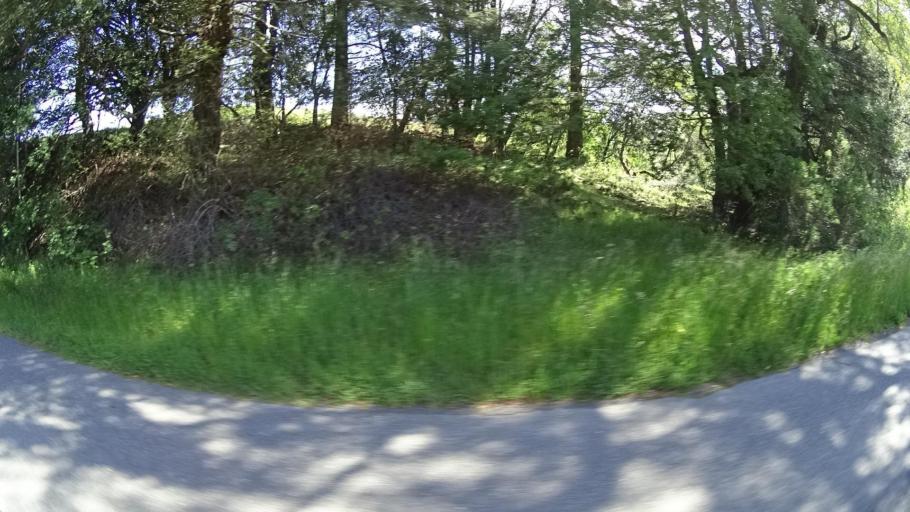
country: US
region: California
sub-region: Humboldt County
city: Ferndale
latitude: 40.3453
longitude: -124.3257
